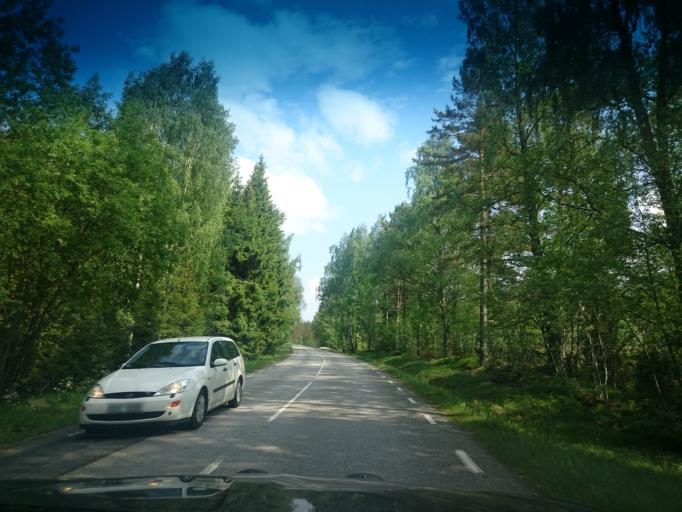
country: SE
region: Joenkoeping
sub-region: Vetlanda Kommun
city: Vetlanda
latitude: 57.3643
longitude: 15.0610
